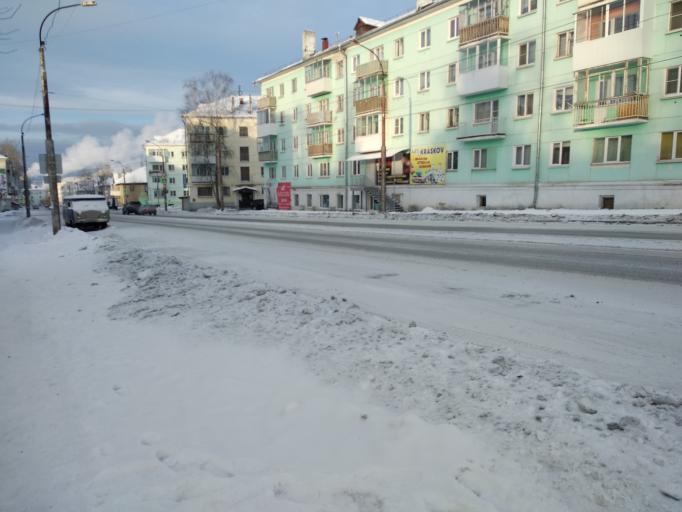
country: RU
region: Sverdlovsk
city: Krasnotur'insk
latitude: 59.7672
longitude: 60.2007
